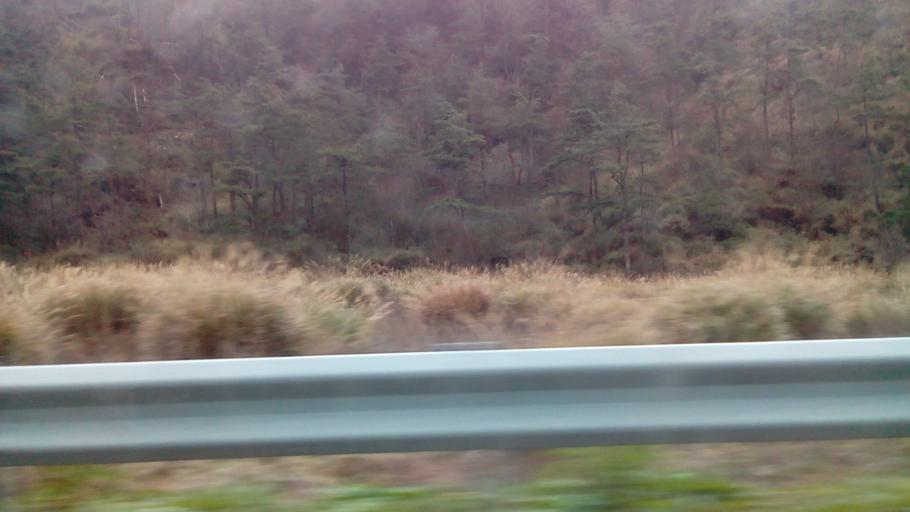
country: TW
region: Taiwan
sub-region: Hualien
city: Hualian
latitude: 24.3900
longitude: 121.3493
